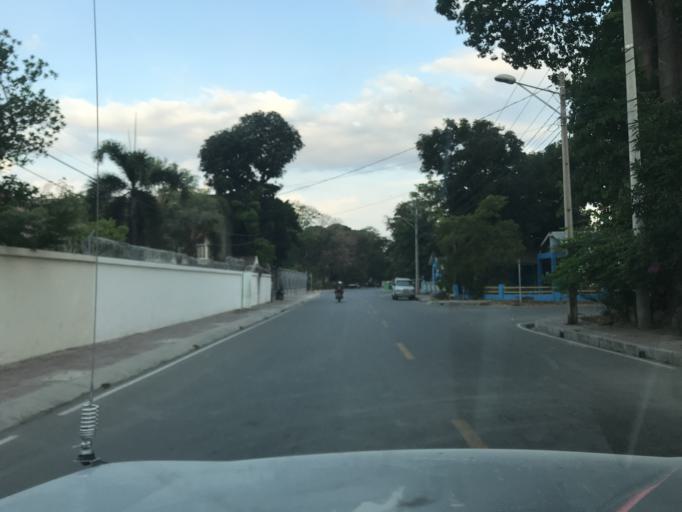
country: TL
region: Dili
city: Dili
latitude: -8.5501
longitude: 125.5671
